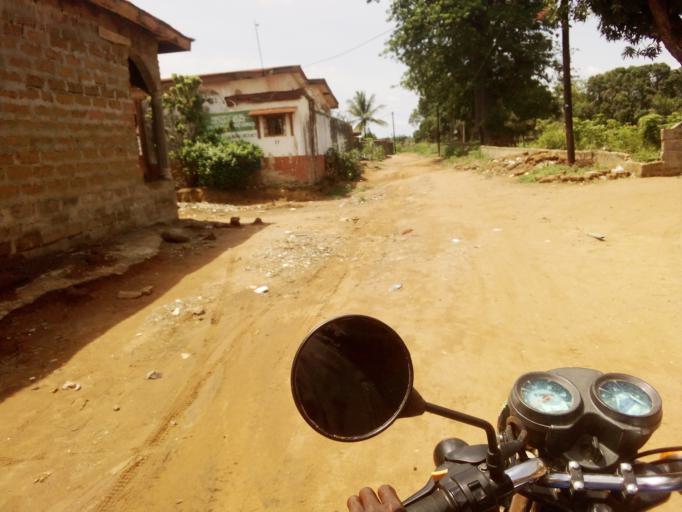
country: SL
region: Western Area
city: Waterloo
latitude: 8.3399
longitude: -13.0673
